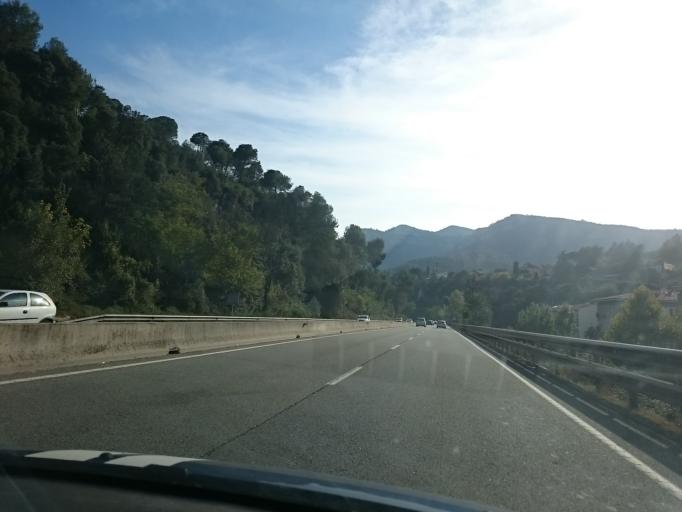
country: ES
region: Catalonia
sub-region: Provincia de Barcelona
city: Aiguafreda
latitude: 41.7613
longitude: 2.2512
